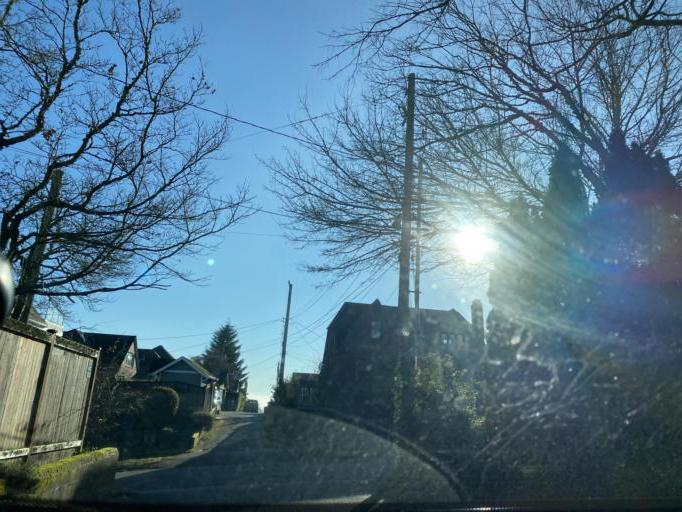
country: US
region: Washington
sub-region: King County
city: Seattle
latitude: 47.6471
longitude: -122.3909
